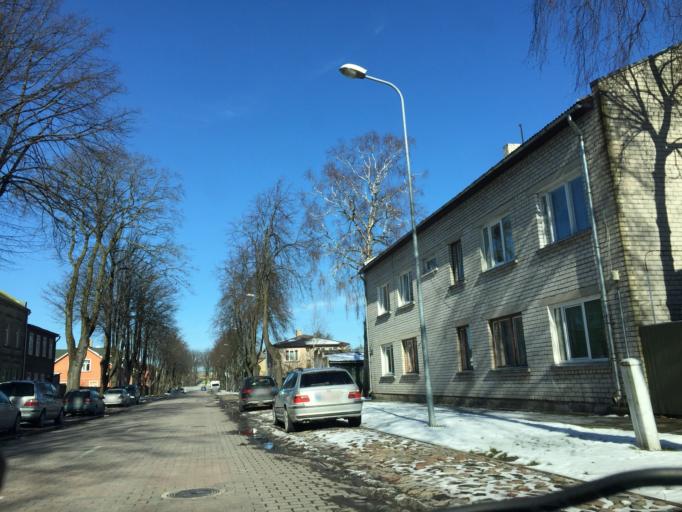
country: LV
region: Ventspils
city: Ventspils
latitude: 57.3901
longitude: 21.5542
